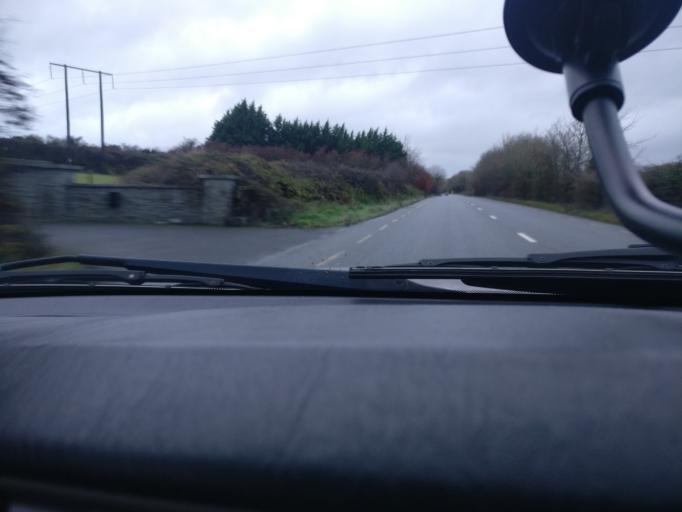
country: IE
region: Leinster
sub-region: Kildare
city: Kilcock
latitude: 53.4156
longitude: -6.7224
